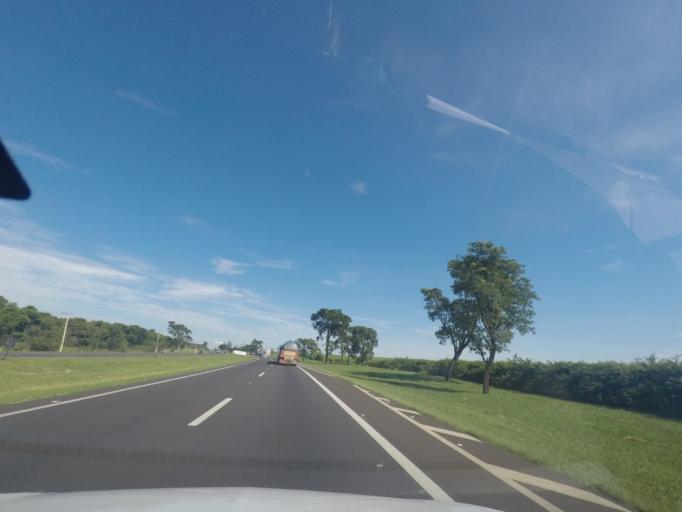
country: BR
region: Sao Paulo
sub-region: Itirapina
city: Itirapina
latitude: -22.2458
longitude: -47.7073
